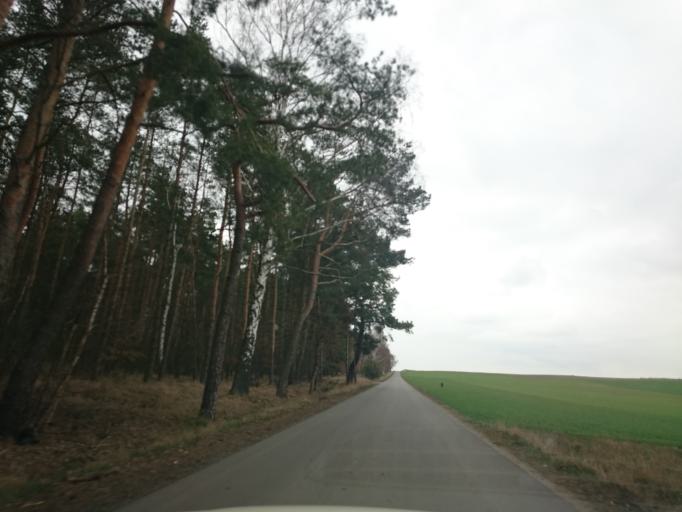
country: PL
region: Kujawsko-Pomorskie
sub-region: Powiat golubsko-dobrzynski
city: Ciechocin
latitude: 53.0487
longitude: 18.8812
